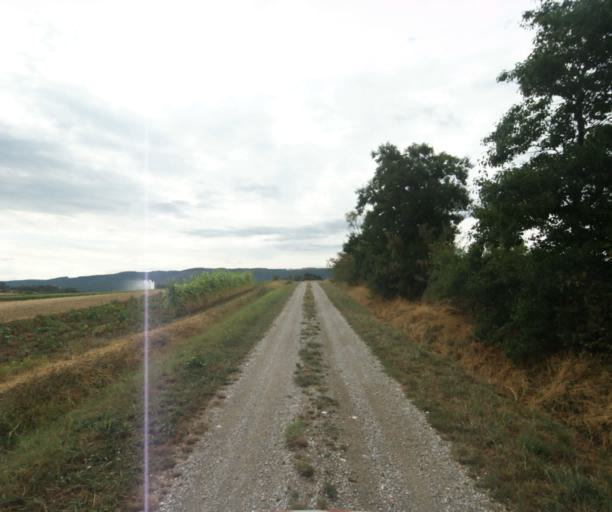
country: FR
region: Midi-Pyrenees
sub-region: Departement de la Haute-Garonne
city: Revel
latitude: 43.4275
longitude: 1.9665
